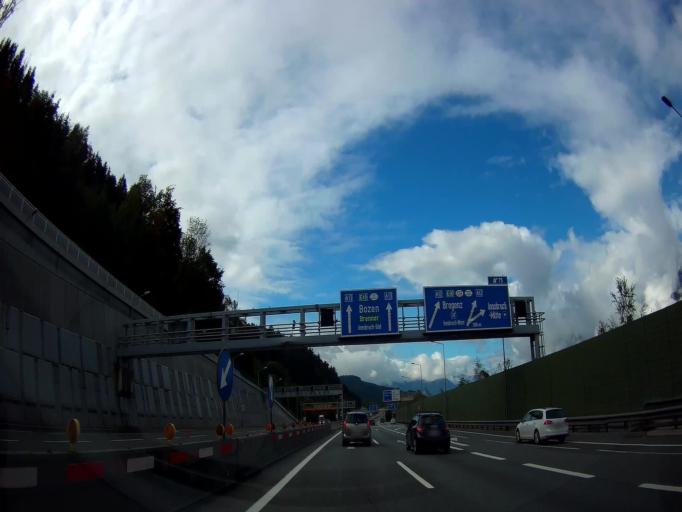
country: AT
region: Tyrol
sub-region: Politischer Bezirk Innsbruck Land
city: Aldrans
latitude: 47.2545
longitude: 11.4222
